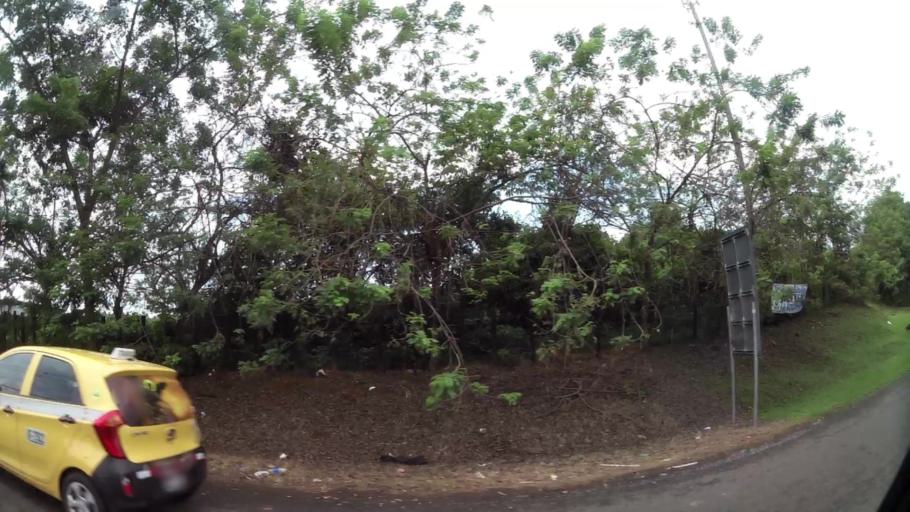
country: PA
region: Panama
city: Cabra Numero Uno
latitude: 9.1133
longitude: -79.3552
